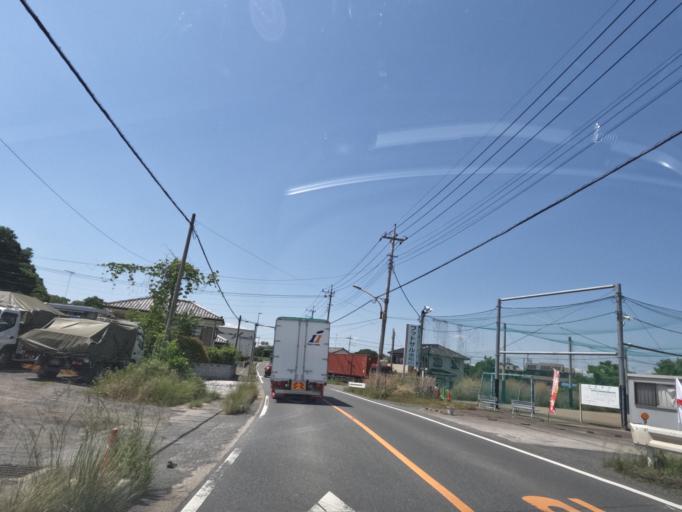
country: JP
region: Saitama
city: Kumagaya
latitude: 36.0919
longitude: 139.4014
